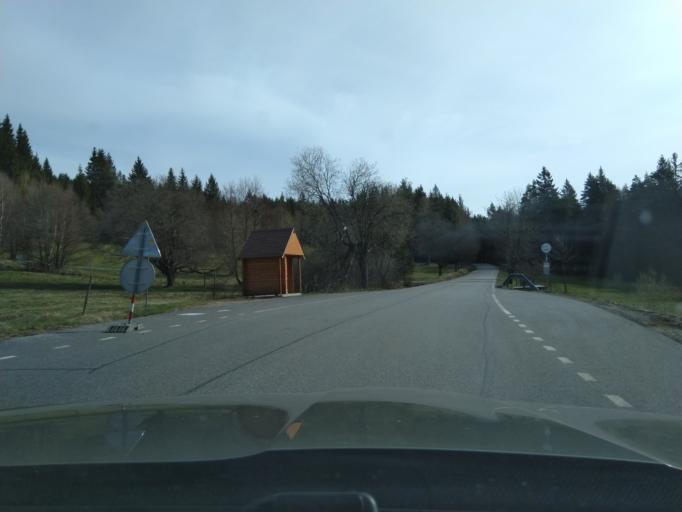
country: CZ
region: Jihocesky
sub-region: Okres Prachatice
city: Stachy
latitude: 49.0785
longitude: 13.6346
